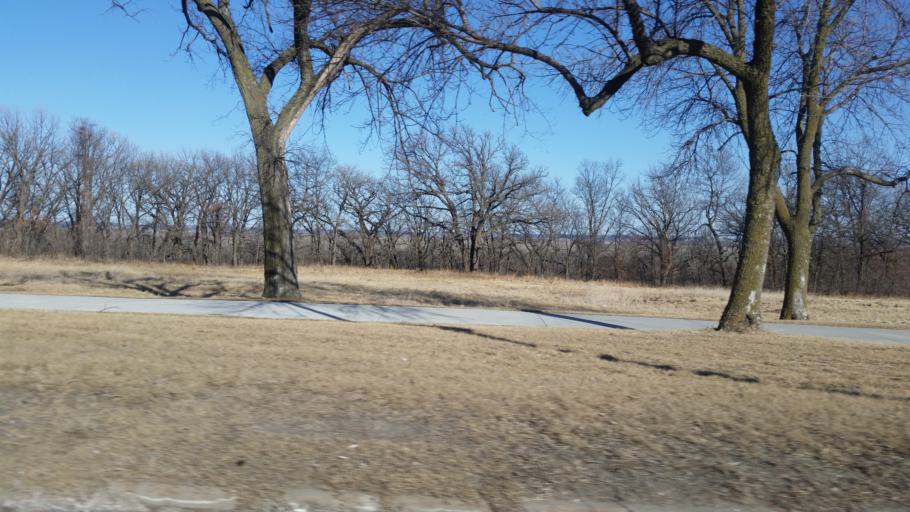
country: US
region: Nebraska
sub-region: Douglas County
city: Omaha
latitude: 41.2028
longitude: -95.9336
